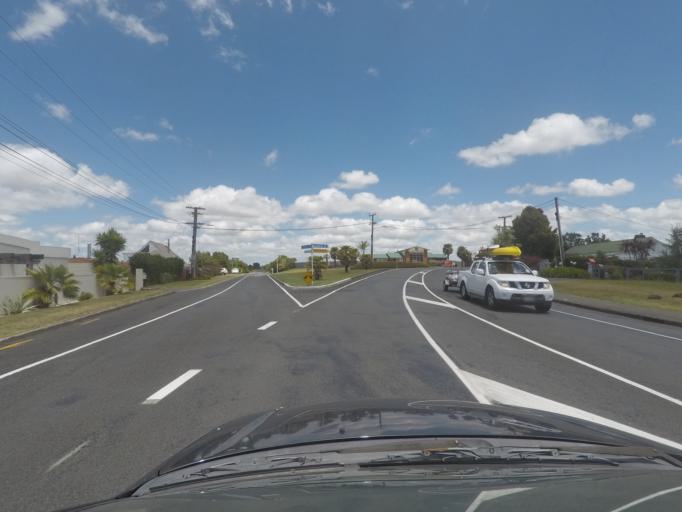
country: NZ
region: Northland
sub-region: Whangarei
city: Whangarei
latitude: -35.7644
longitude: 174.3672
